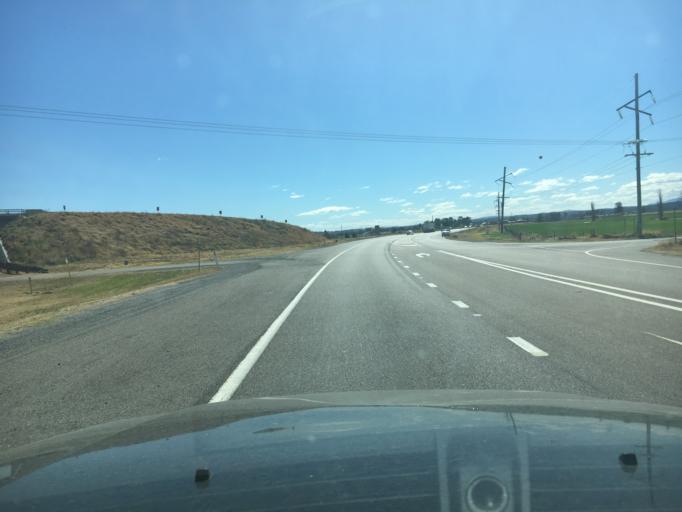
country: AU
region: New South Wales
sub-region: Singleton
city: Singleton
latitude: -32.6050
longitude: 151.2017
